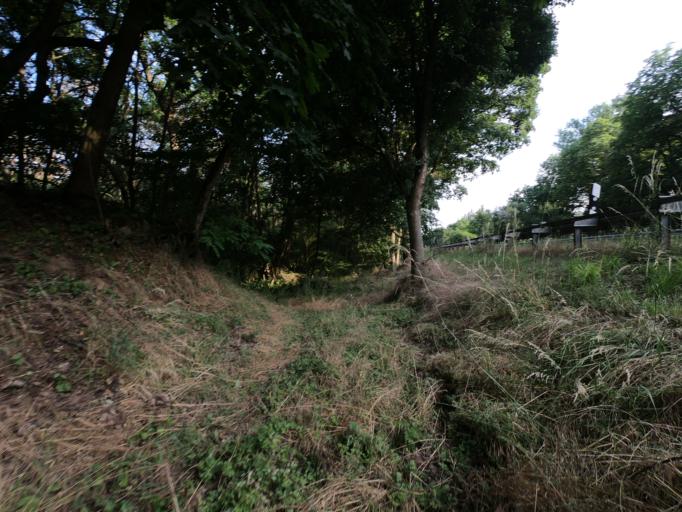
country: DE
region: Hesse
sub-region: Regierungsbezirk Darmstadt
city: Russelsheim
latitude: 49.9664
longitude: 8.4141
